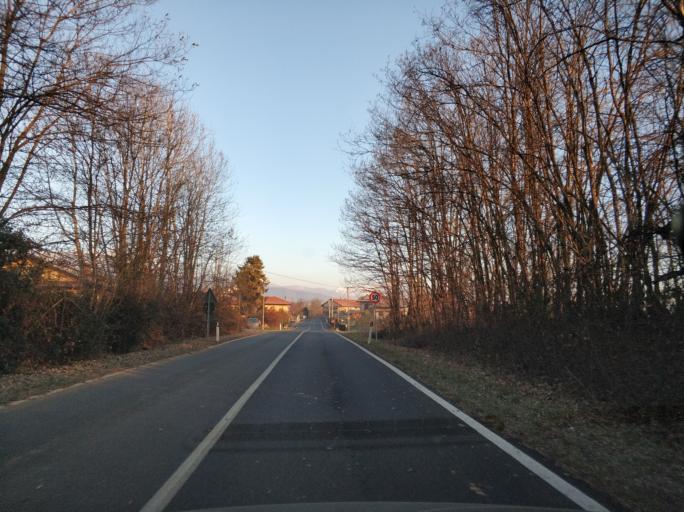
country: IT
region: Piedmont
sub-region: Provincia di Torino
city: Rocca Canavese
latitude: 45.2787
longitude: 7.5817
